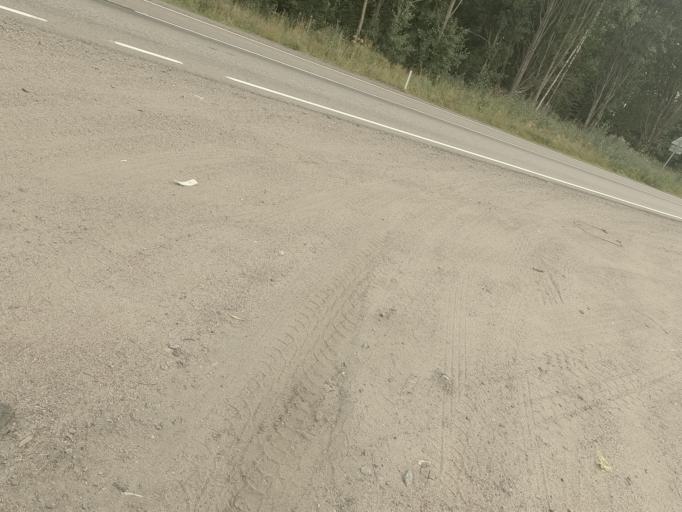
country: RU
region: Leningrad
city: Kamennogorsk
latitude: 60.8778
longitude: 29.0104
